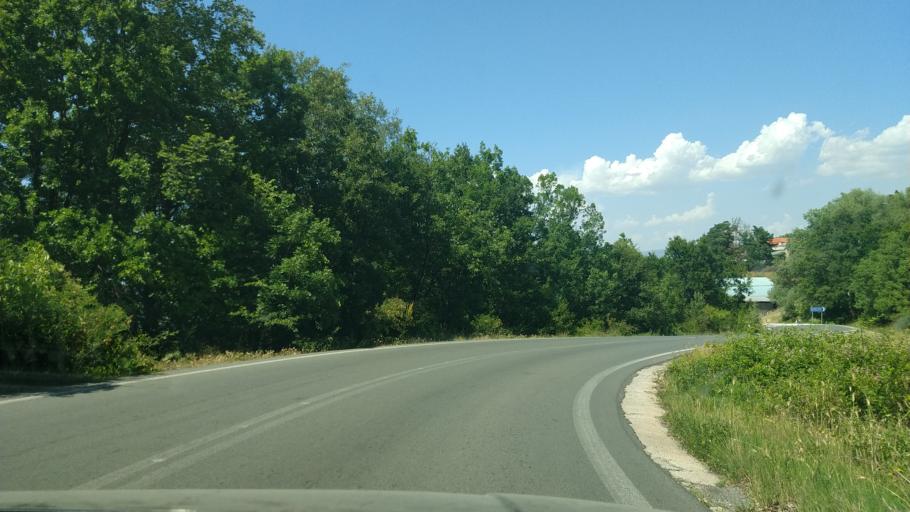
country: GR
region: West Macedonia
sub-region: Nomos Grevenon
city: Grevena
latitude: 40.0347
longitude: 21.4817
